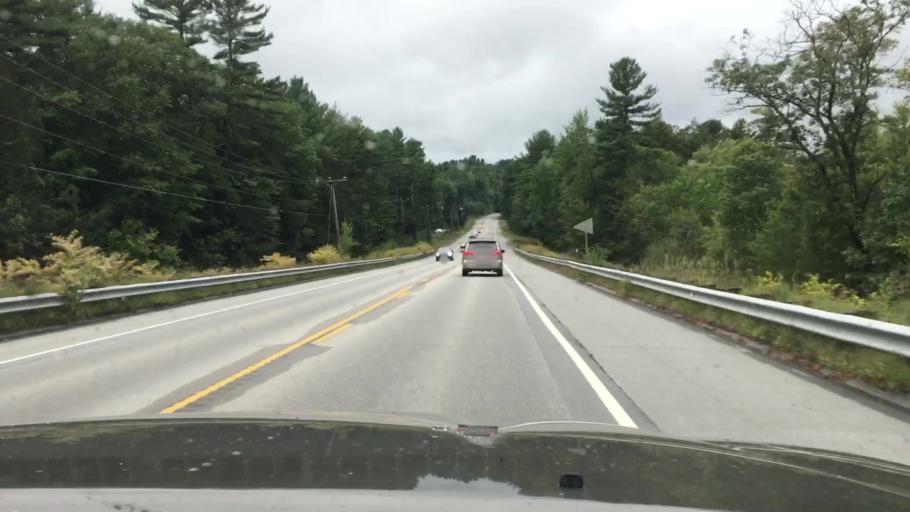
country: US
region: New Hampshire
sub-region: Cheshire County
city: Chesterfield
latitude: 42.8990
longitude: -72.4385
